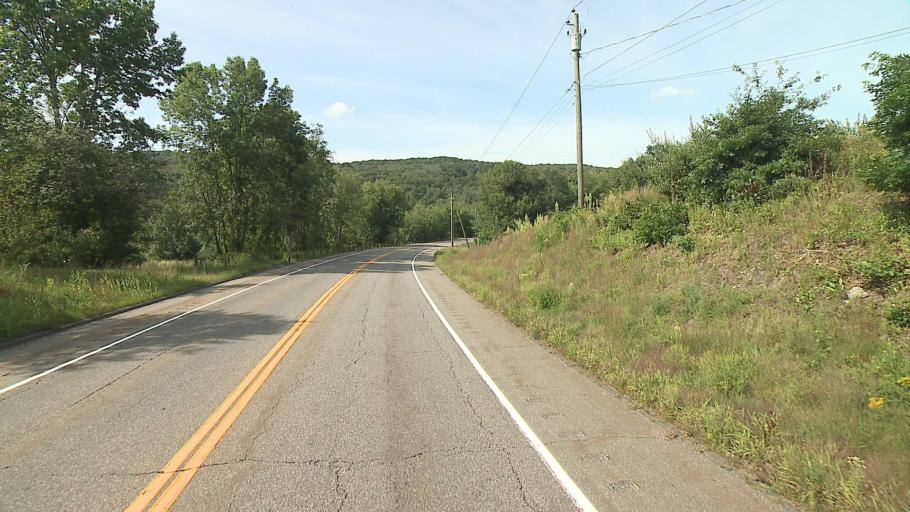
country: US
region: Connecticut
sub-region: Litchfield County
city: Torrington
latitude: 41.7626
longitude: -73.1337
